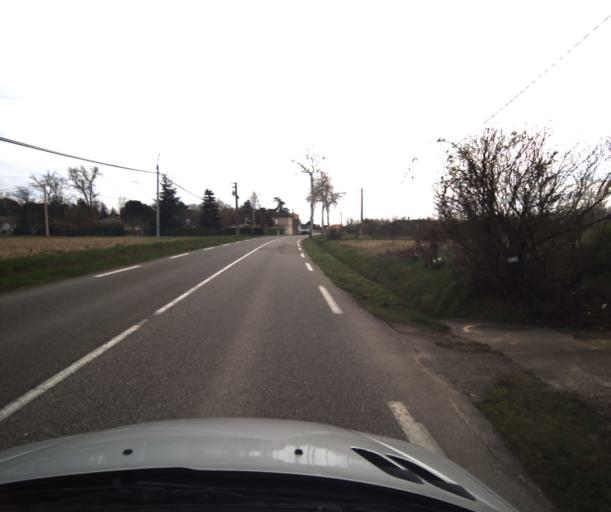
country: FR
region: Midi-Pyrenees
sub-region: Departement du Tarn-et-Garonne
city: Montbeton
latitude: 44.0483
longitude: 1.2976
